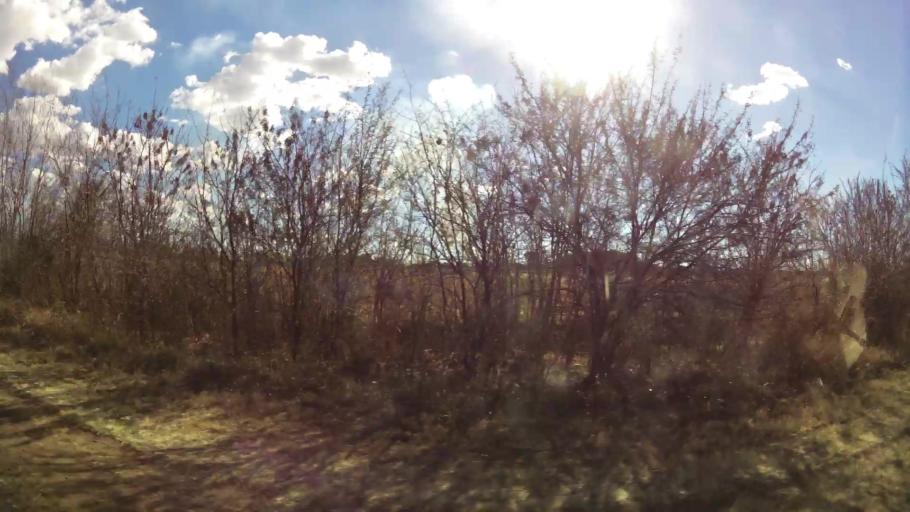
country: ZA
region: North-West
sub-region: Dr Kenneth Kaunda District Municipality
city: Klerksdorp
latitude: -26.8497
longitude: 26.6503
